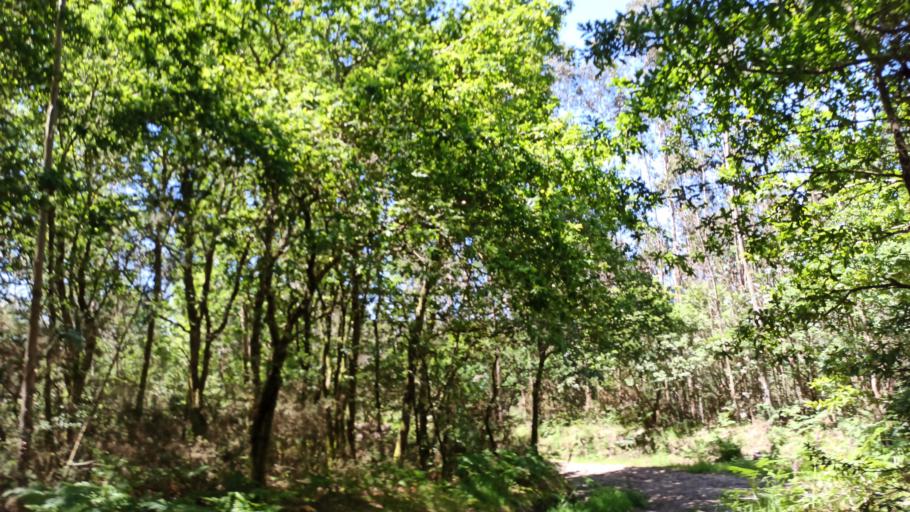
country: ES
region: Galicia
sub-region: Provincia da Coruna
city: Negreira
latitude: 42.9226
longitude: -8.7166
